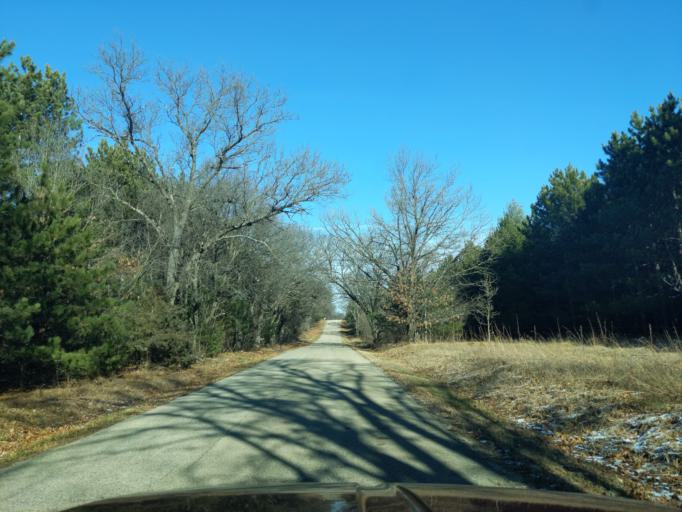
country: US
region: Wisconsin
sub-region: Waushara County
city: Silver Lake
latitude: 44.1065
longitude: -89.1689
